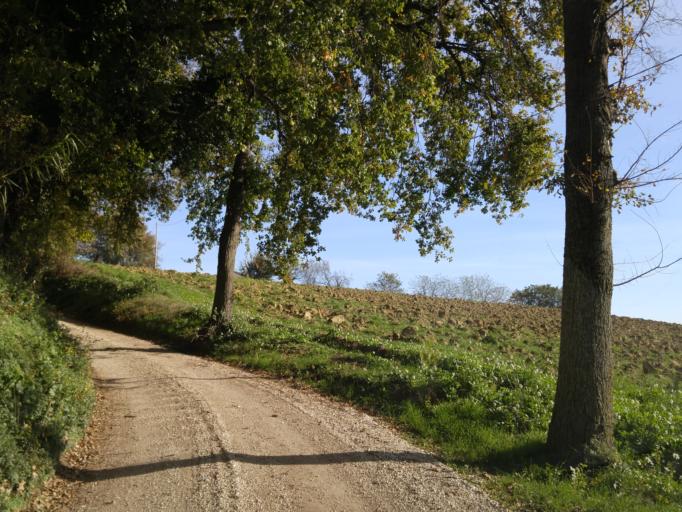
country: IT
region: The Marches
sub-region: Provincia di Pesaro e Urbino
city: Saltara
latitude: 43.7640
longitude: 12.9034
